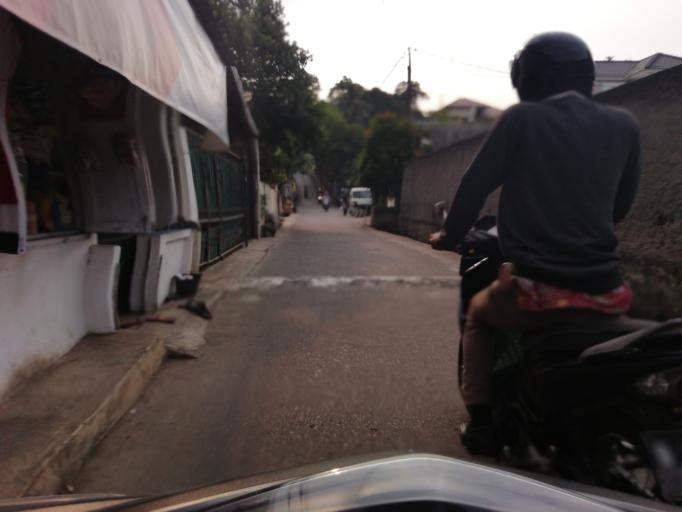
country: ID
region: West Java
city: Pamulang
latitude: -6.3069
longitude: 106.8077
